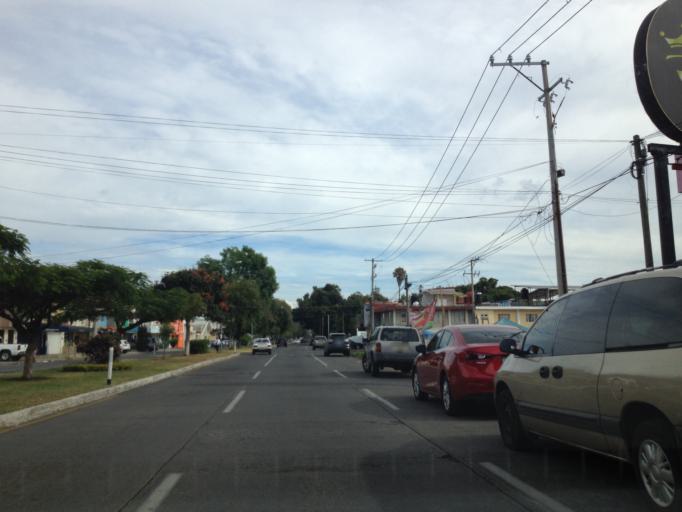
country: MX
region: Michoacan
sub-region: Uruapan
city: Uruapan
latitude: 19.4049
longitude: -102.0487
